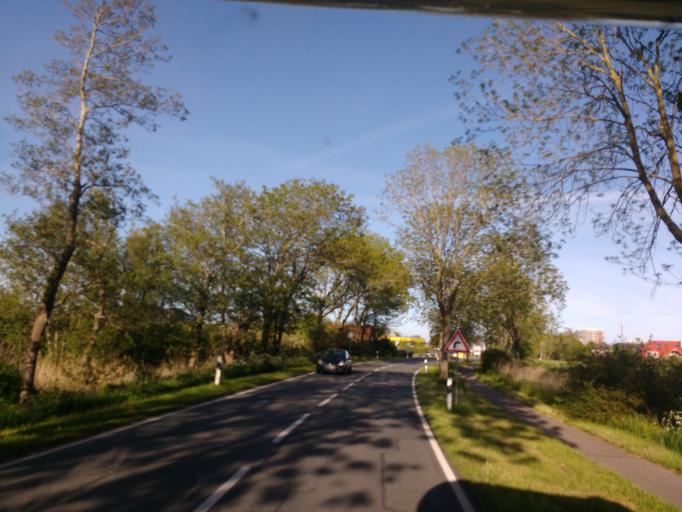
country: DE
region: Lower Saxony
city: Schillig
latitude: 53.6855
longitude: 8.0035
